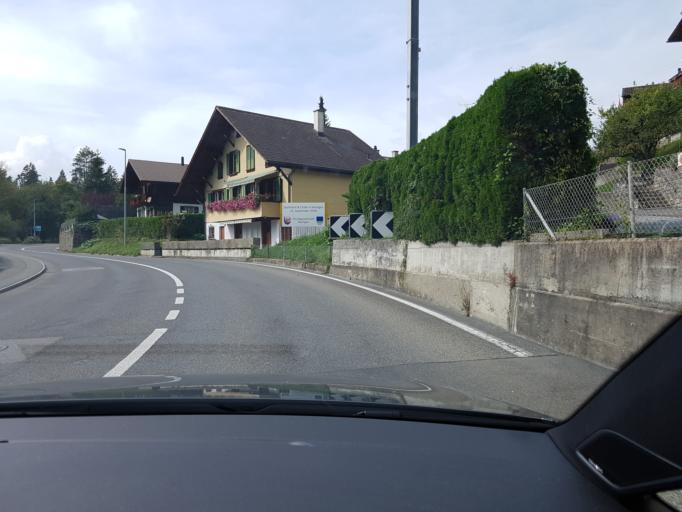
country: CH
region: Bern
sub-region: Thun District
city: Sigriswil
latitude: 46.6947
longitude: 7.7419
